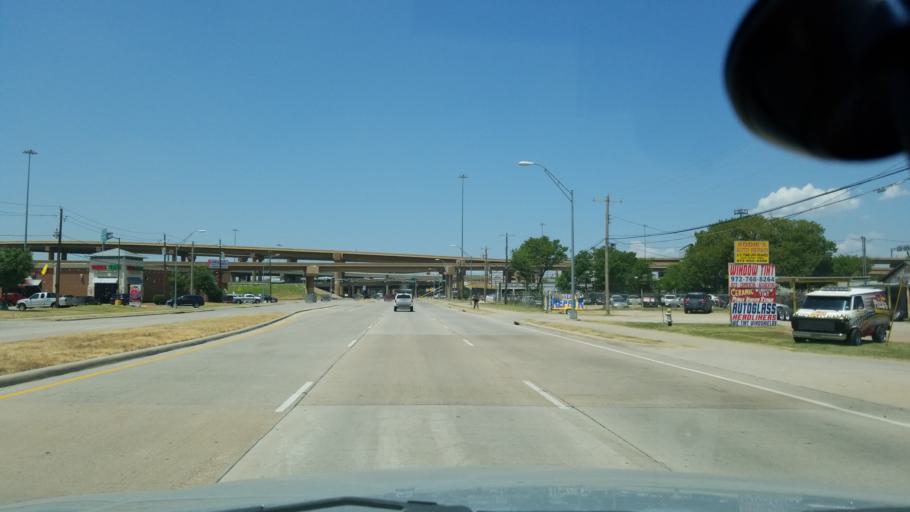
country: US
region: Texas
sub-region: Dallas County
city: Farmers Branch
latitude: 32.9049
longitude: -96.8941
